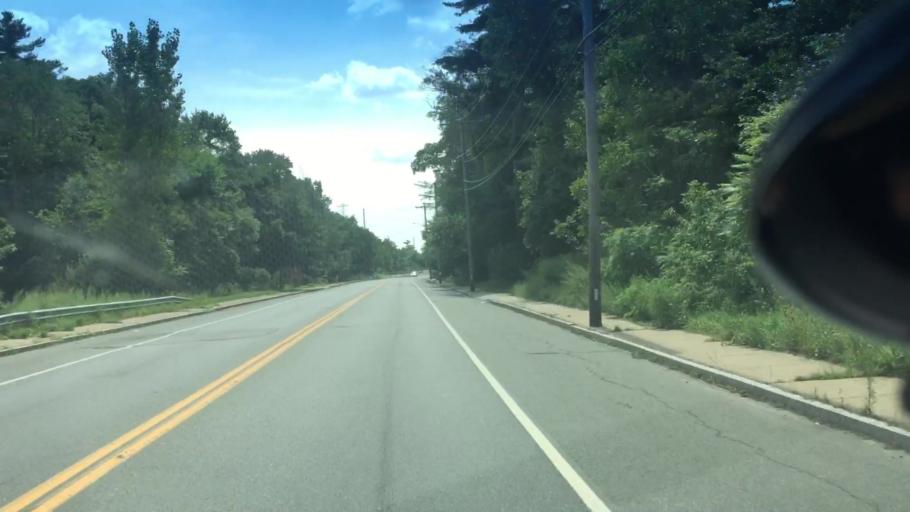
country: US
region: Massachusetts
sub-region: Norfolk County
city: Stoughton
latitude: 42.1475
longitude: -71.0751
